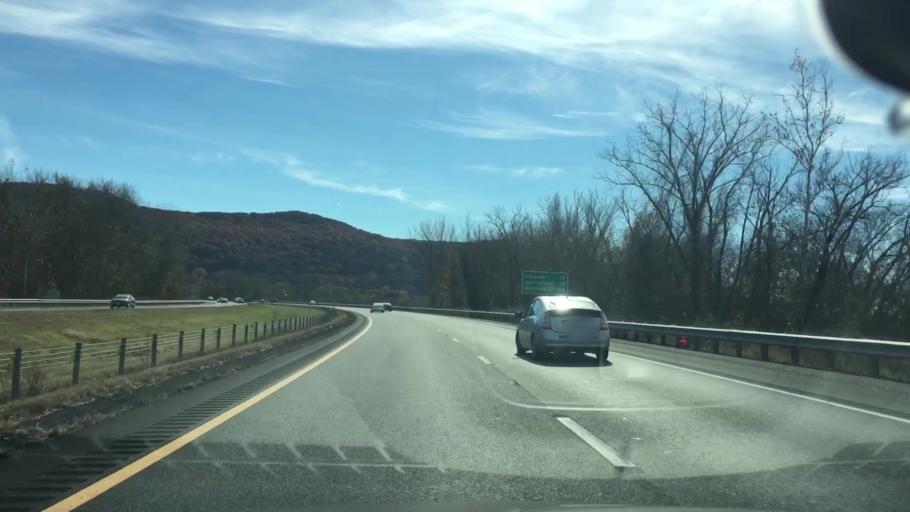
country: US
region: Massachusetts
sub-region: Hampshire County
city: Northampton
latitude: 42.2967
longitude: -72.6300
